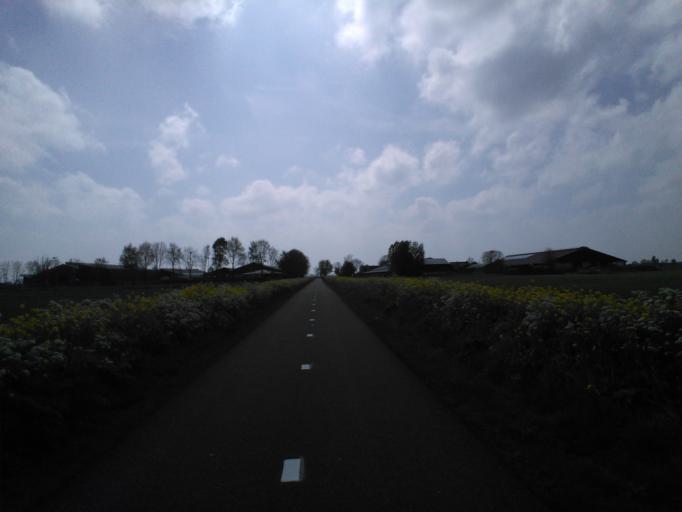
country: NL
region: South Holland
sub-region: Gemeente Leiderdorp
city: Leiderdorp
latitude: 52.1240
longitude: 4.5480
